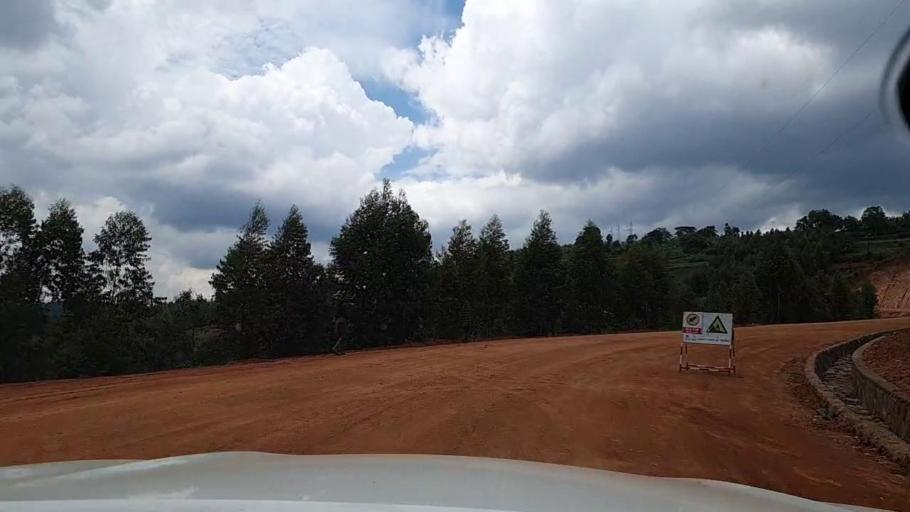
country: RW
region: Southern Province
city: Butare
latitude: -2.7026
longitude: 29.5551
